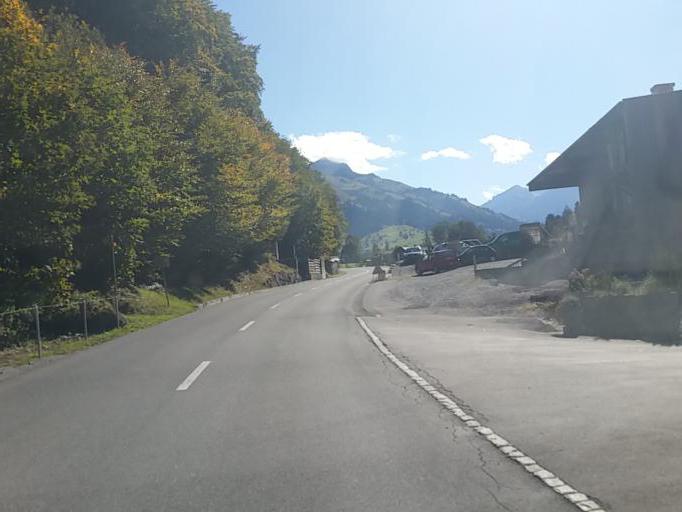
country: CH
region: Bern
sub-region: Frutigen-Niedersimmental District
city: Aeschi
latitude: 46.6430
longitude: 7.6928
